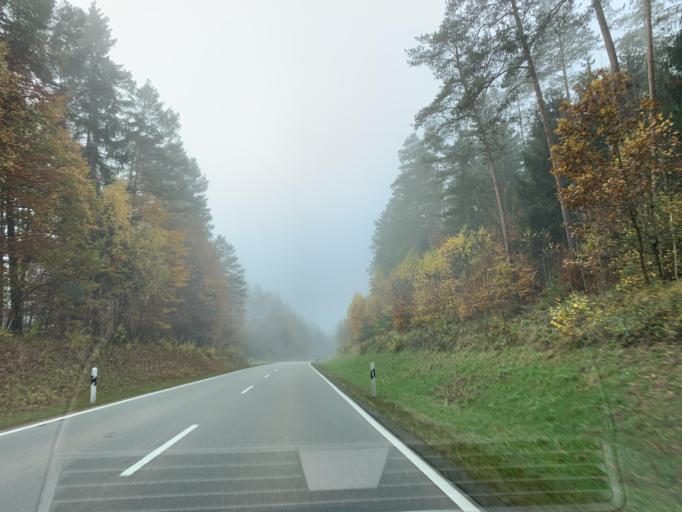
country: DE
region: Bavaria
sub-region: Upper Palatinate
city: Brunn
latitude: 49.2349
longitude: 12.1719
